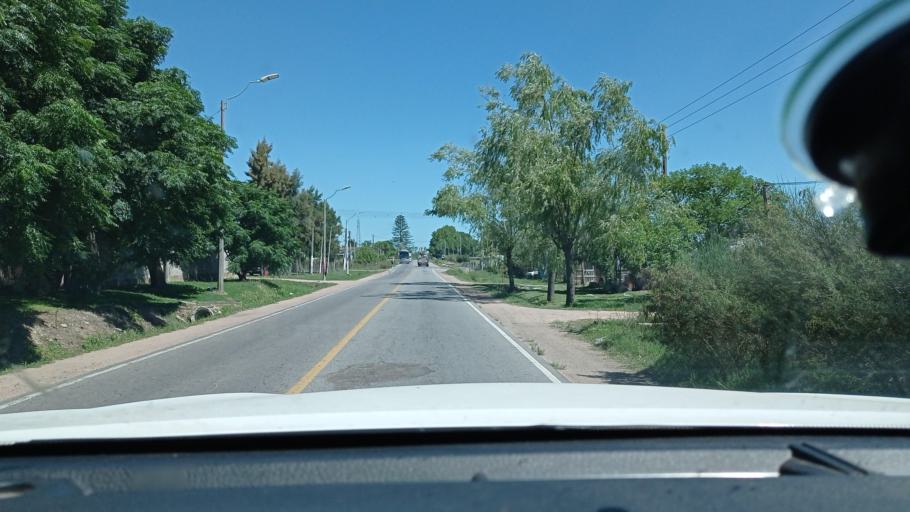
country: UY
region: Canelones
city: La Paz
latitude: -34.7766
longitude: -56.1671
